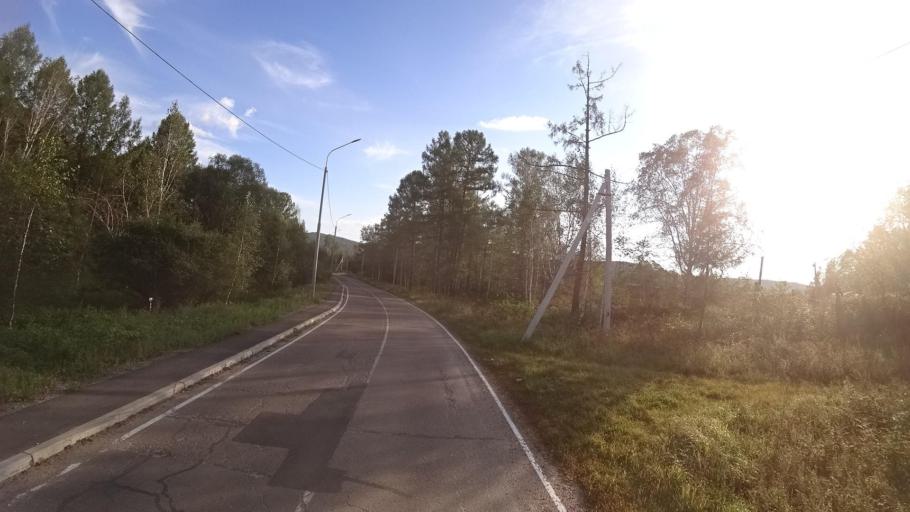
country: RU
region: Jewish Autonomous Oblast
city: Kul'dur
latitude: 49.2053
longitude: 131.6207
